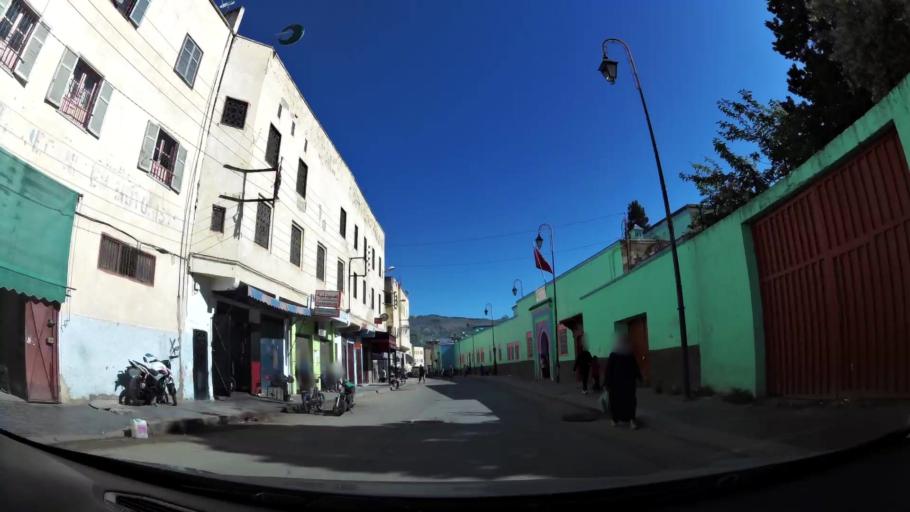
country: MA
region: Fes-Boulemane
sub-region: Fes
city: Fes
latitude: 34.0617
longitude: -4.9644
